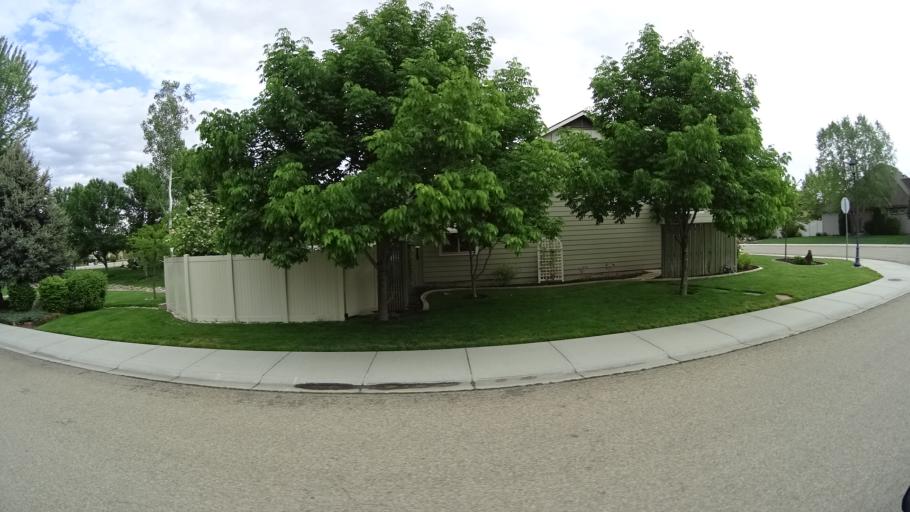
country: US
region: Idaho
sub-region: Ada County
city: Star
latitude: 43.6877
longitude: -116.5013
